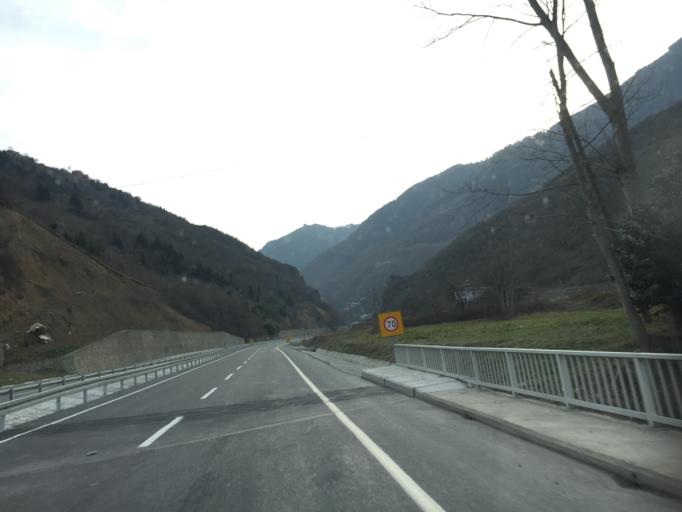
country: TR
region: Trabzon
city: Macka
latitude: 40.7871
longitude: 39.5778
